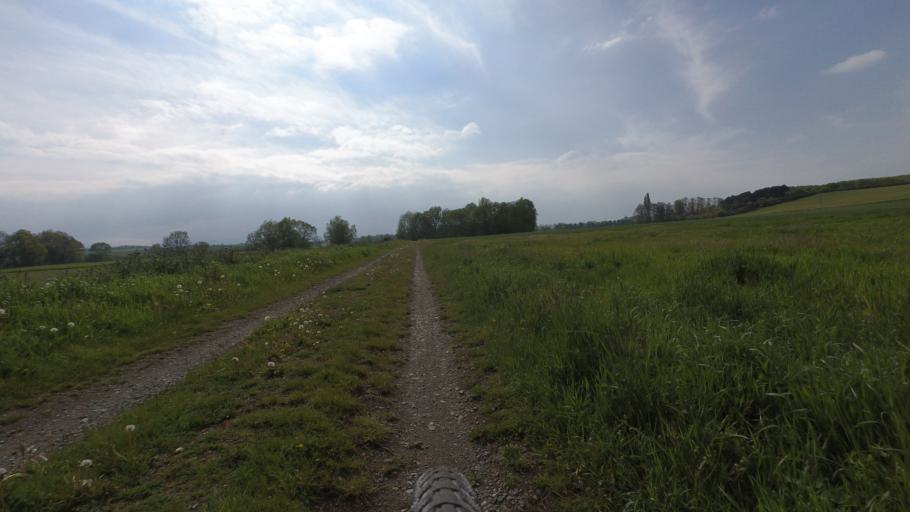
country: DE
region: Saxony-Anhalt
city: Strobeck
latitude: 51.8833
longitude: 10.9410
